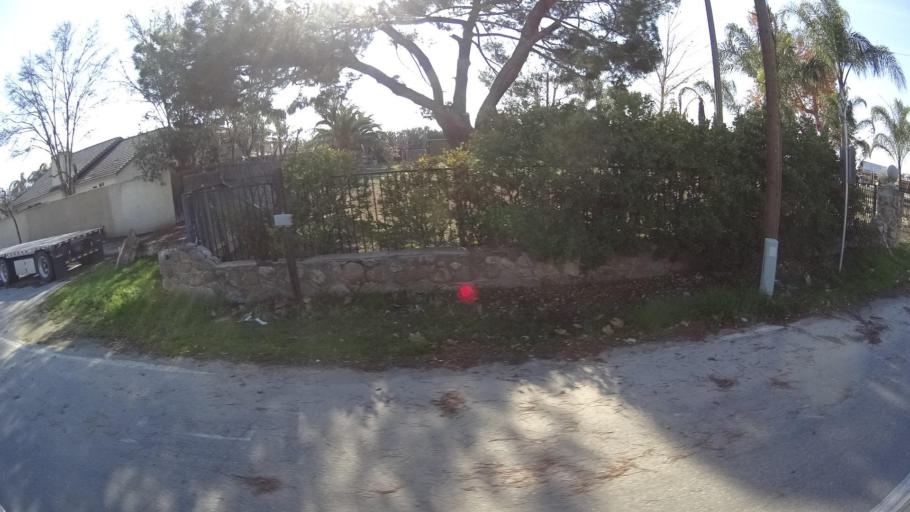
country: US
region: California
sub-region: Kern County
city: Arvin
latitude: 35.1945
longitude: -118.8324
